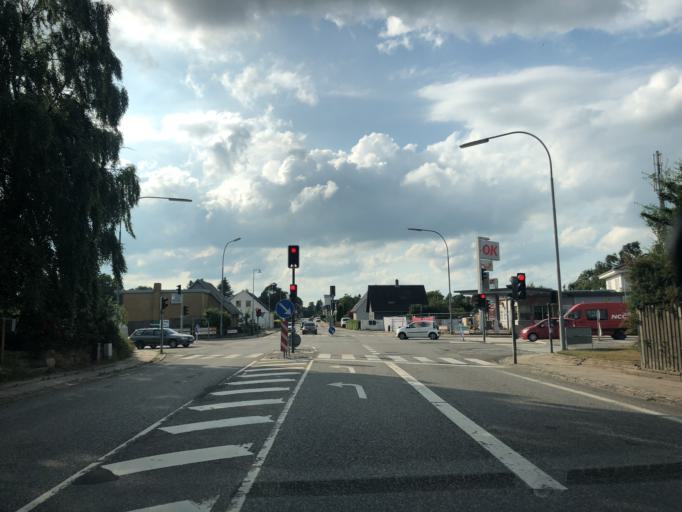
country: DK
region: Zealand
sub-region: Faxe Kommune
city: Haslev
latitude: 55.3188
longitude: 11.9739
